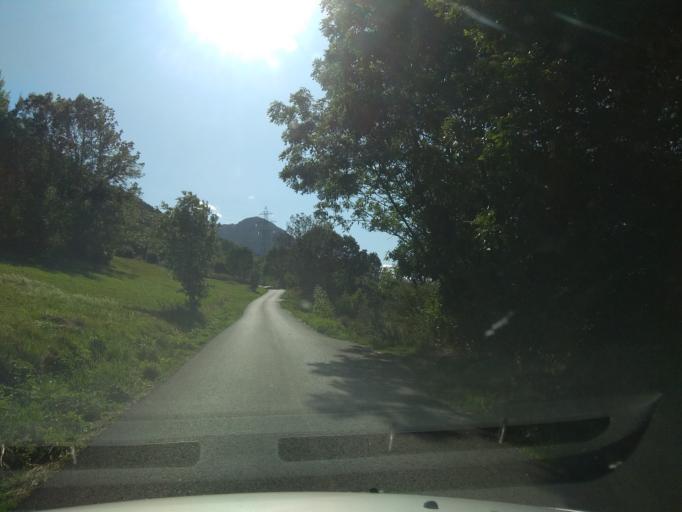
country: ES
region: Catalonia
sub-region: Provincia de Lleida
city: Vielha
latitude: 42.7023
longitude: 0.9064
